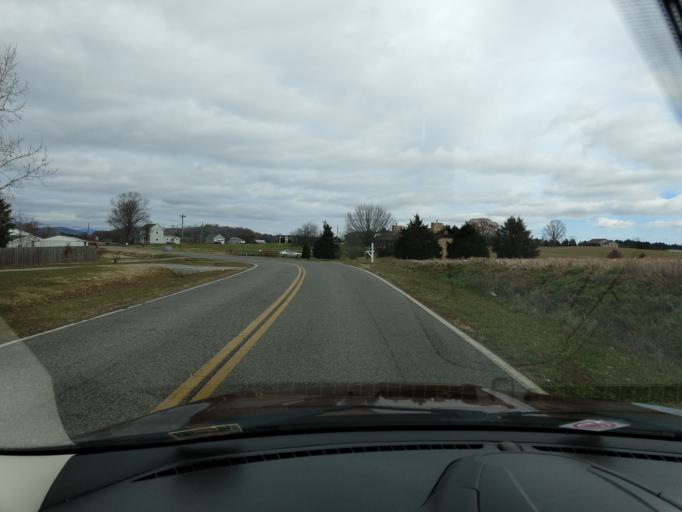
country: US
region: Virginia
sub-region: Franklin County
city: North Shore
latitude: 37.2299
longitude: -79.6740
